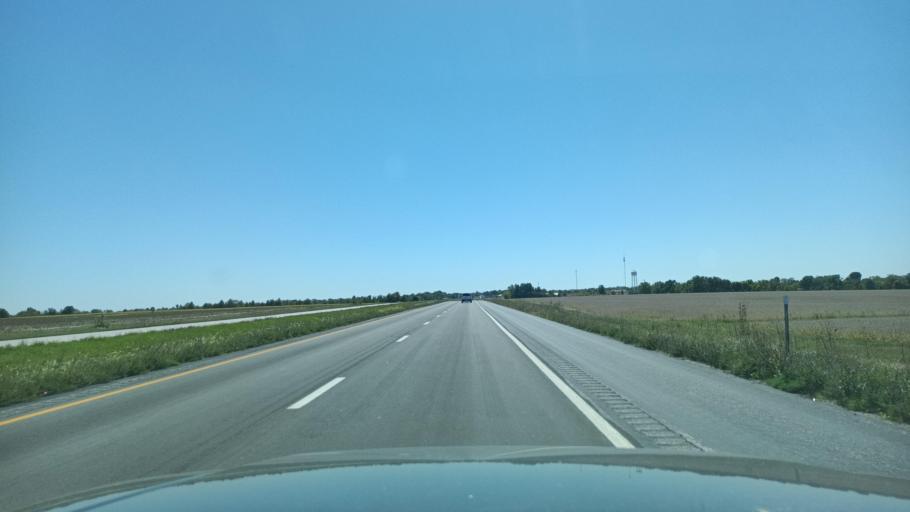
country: US
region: Missouri
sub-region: Macon County
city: La Plata
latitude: 40.0501
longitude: -92.4946
